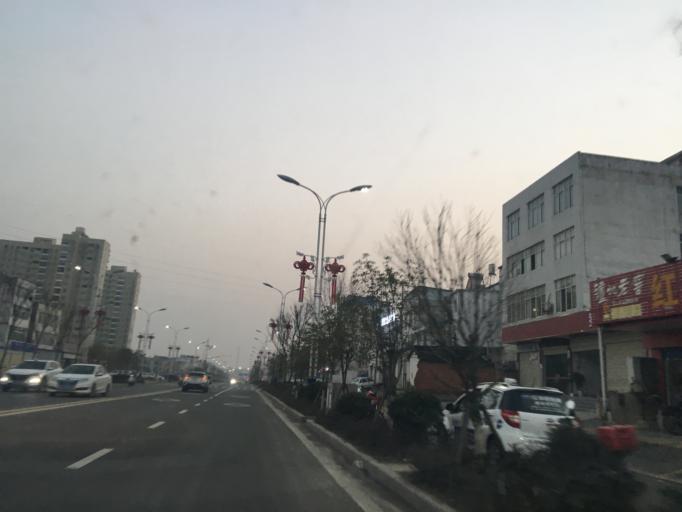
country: CN
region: Hubei
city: Macheng
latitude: 31.1675
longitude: 115.0208
